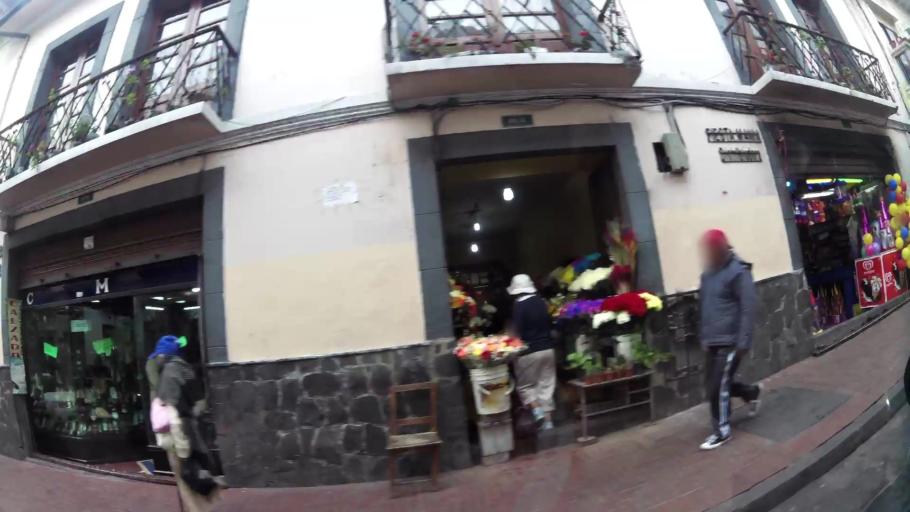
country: EC
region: Pichincha
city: Quito
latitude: -0.2218
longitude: -78.5154
